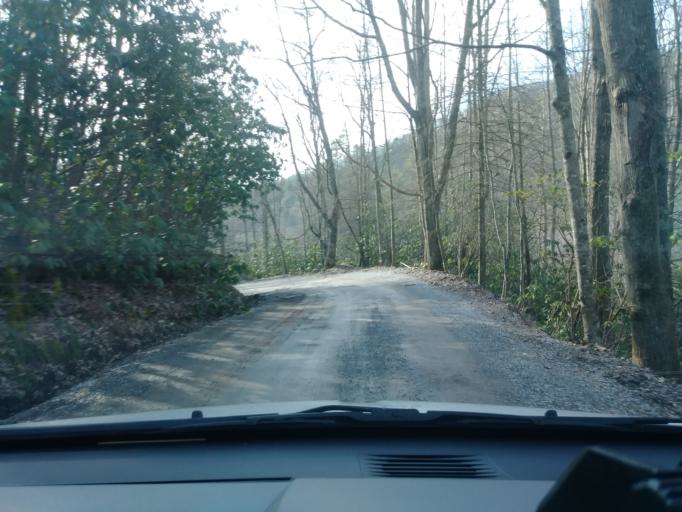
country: US
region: Tennessee
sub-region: Greene County
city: Tusculum
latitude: 36.0280
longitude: -82.7274
